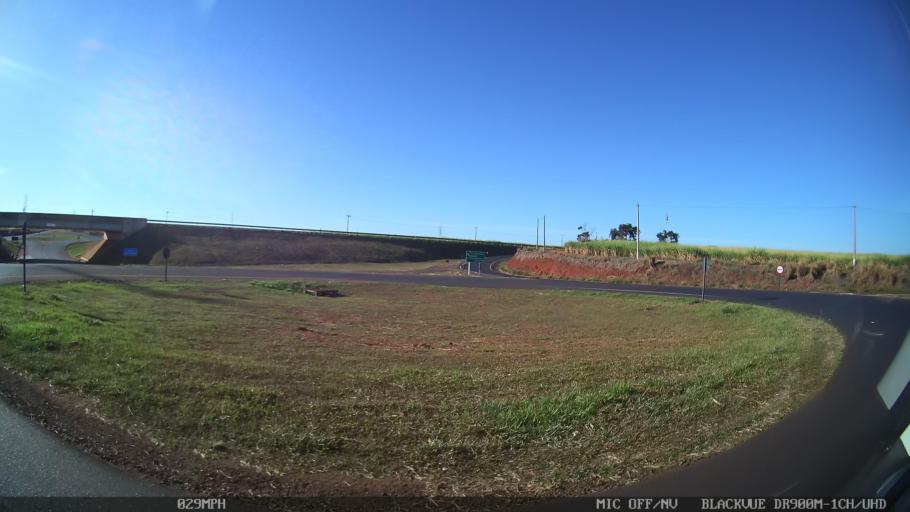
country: BR
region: Sao Paulo
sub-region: Guapiacu
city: Guapiacu
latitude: -20.7375
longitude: -49.0802
